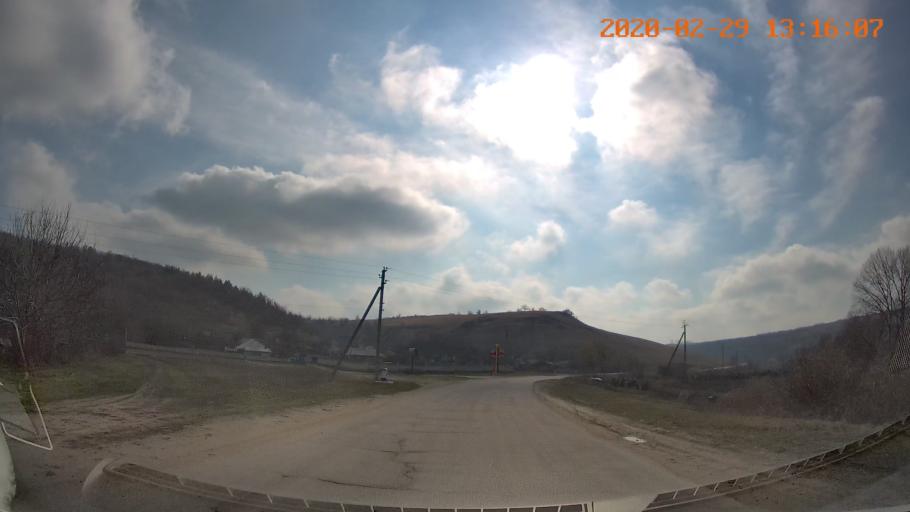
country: MD
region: Telenesti
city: Camenca
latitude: 48.0049
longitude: 28.6665
